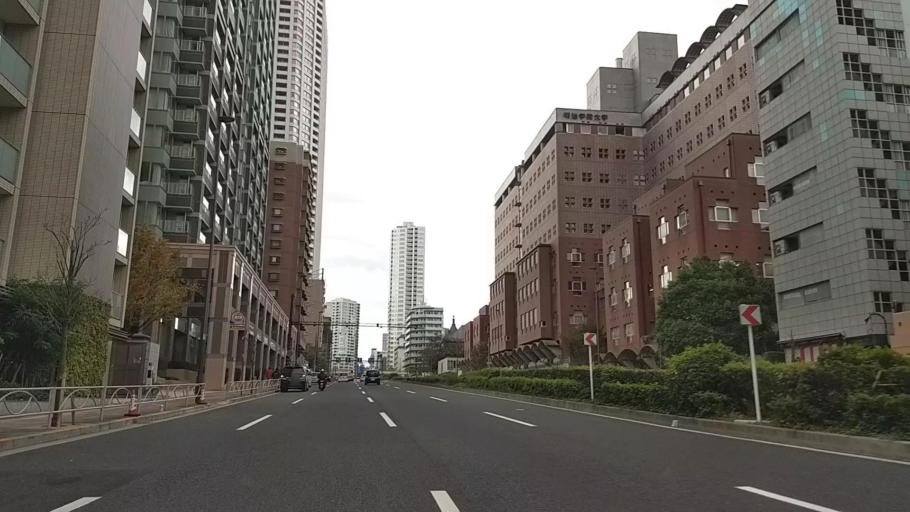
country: JP
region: Tokyo
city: Tokyo
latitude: 35.6387
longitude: 139.7319
